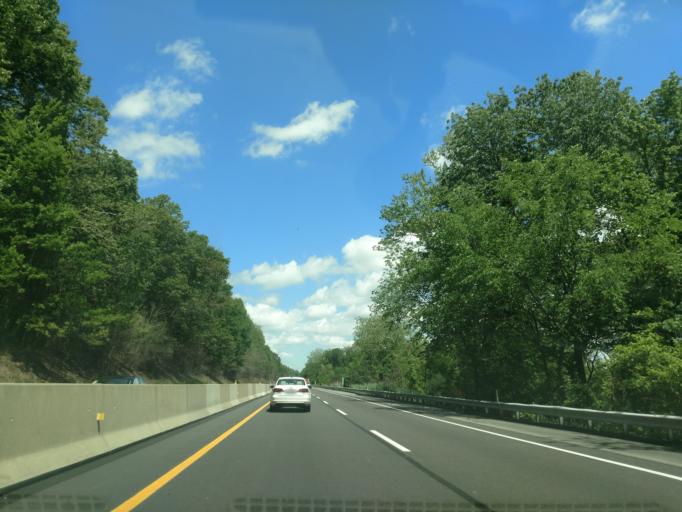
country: US
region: Pennsylvania
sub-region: Chester County
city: Malvern
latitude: 40.0743
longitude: -75.5131
